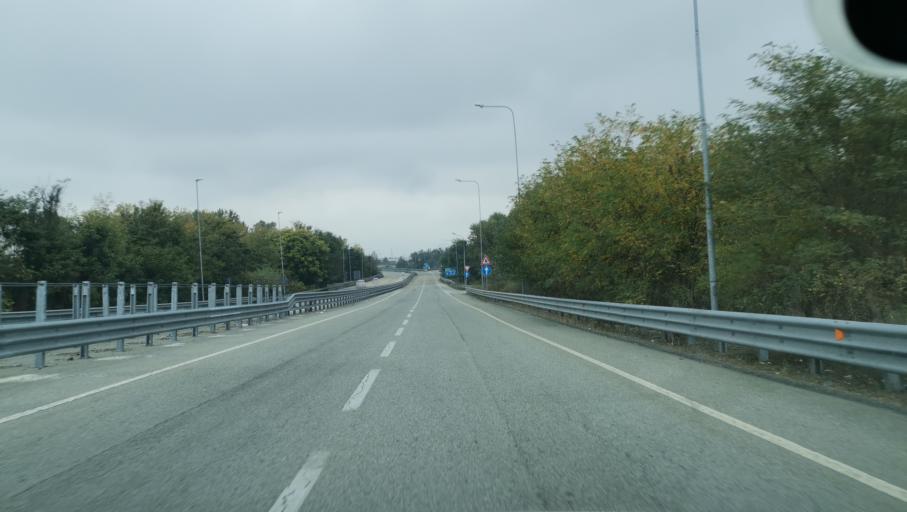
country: IT
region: Piedmont
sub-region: Provincia di Torino
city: Brandizzo
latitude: 45.1623
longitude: 7.8222
